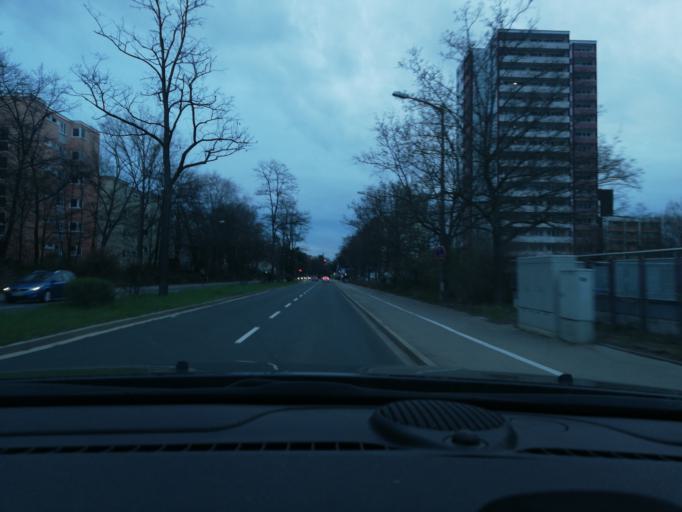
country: DE
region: Bavaria
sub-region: Regierungsbezirk Mittelfranken
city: Erlangen
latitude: 49.5909
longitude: 10.9697
